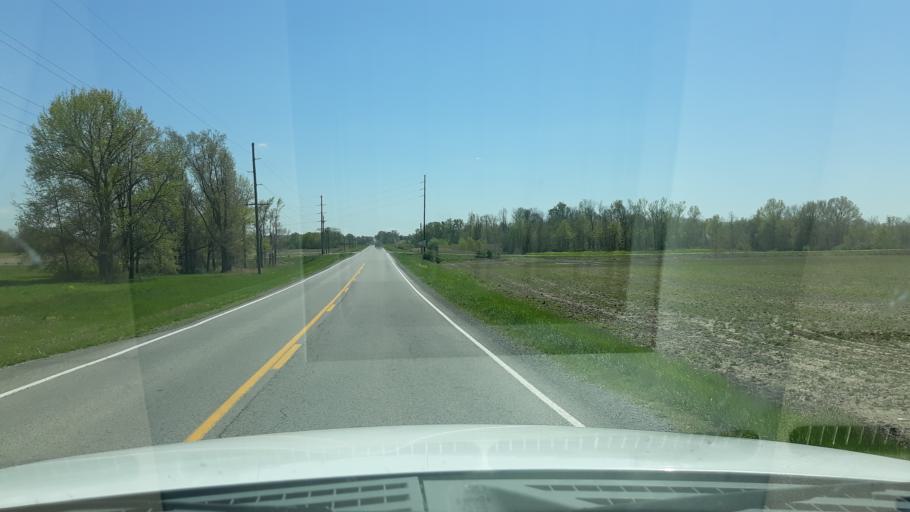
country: US
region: Illinois
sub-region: Saline County
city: Harrisburg
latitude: 37.8361
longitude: -88.6517
